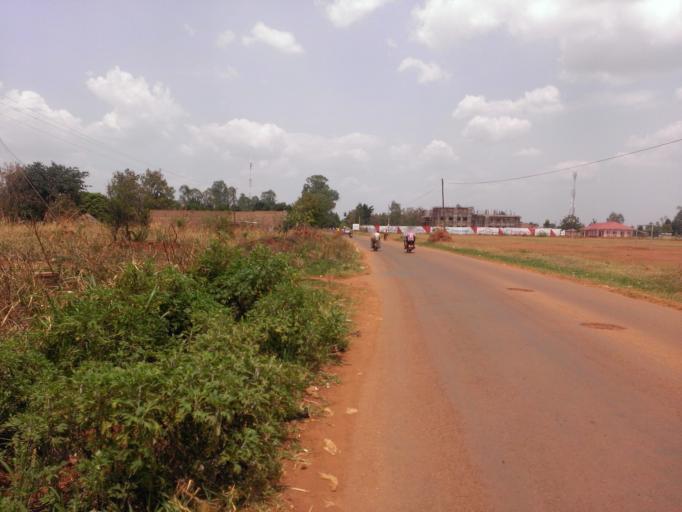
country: UG
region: Northern Region
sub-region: Gulu District
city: Gulu
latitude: 2.7845
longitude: 32.3106
